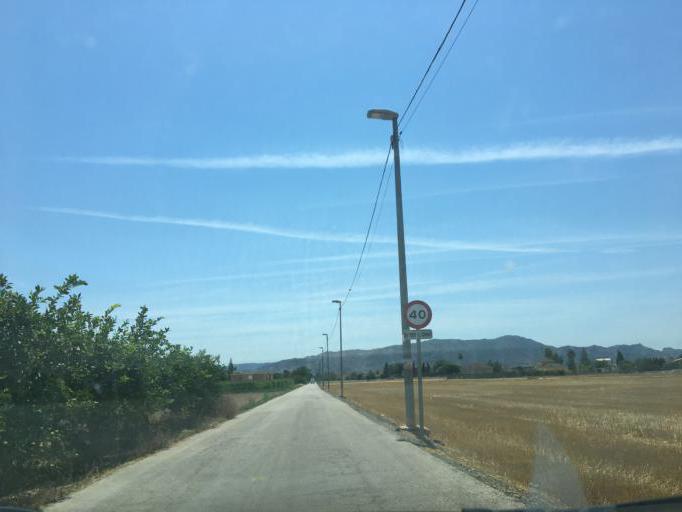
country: ES
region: Murcia
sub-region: Murcia
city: Santomera
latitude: 38.0283
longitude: -1.0623
